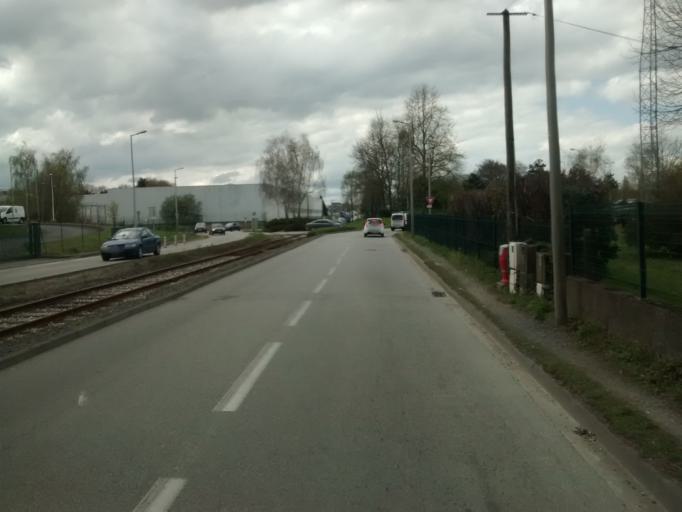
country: FR
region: Brittany
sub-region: Departement du Morbihan
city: Vannes
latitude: 47.6632
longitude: -2.7253
